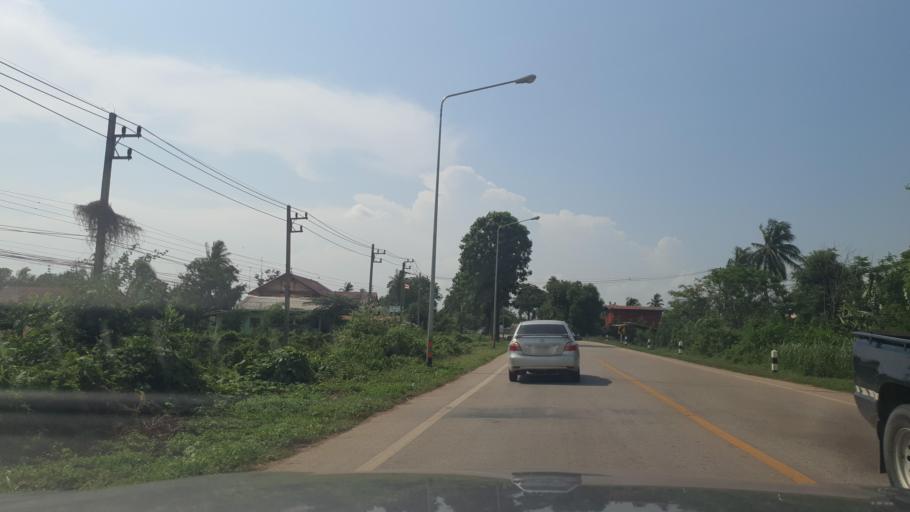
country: TH
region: Sukhothai
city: Si Samrong
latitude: 17.1923
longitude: 99.8508
